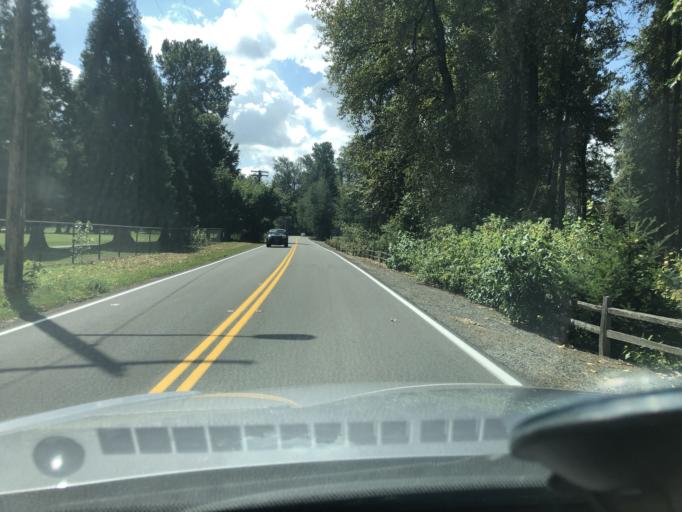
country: US
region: Washington
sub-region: King County
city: Lea Hill
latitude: 47.3350
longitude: -122.2095
